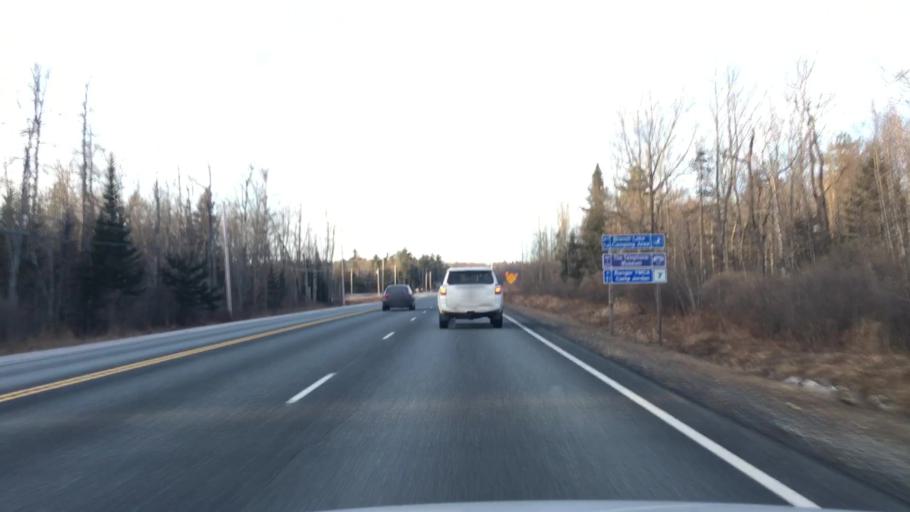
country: US
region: Maine
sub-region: Hancock County
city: Dedham
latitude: 44.6418
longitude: -68.5528
